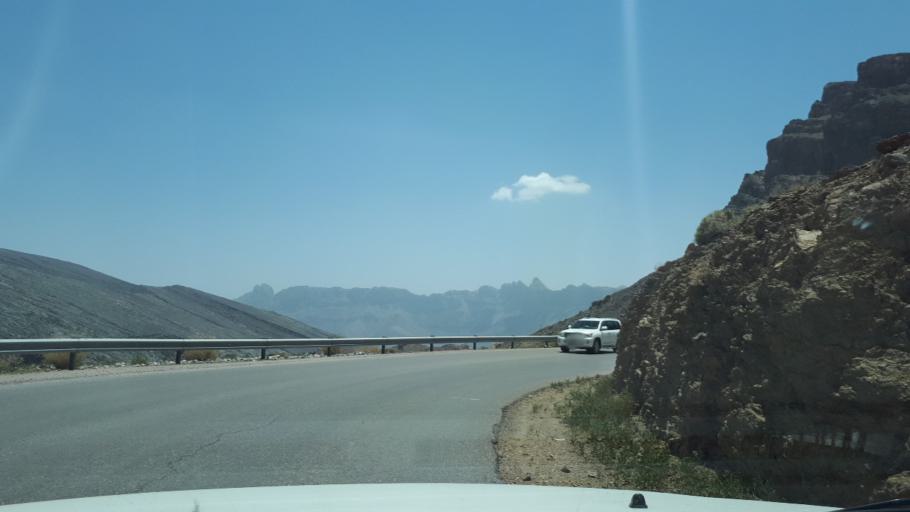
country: OM
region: Muhafazat ad Dakhiliyah
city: Bahla'
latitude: 23.2273
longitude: 57.1454
